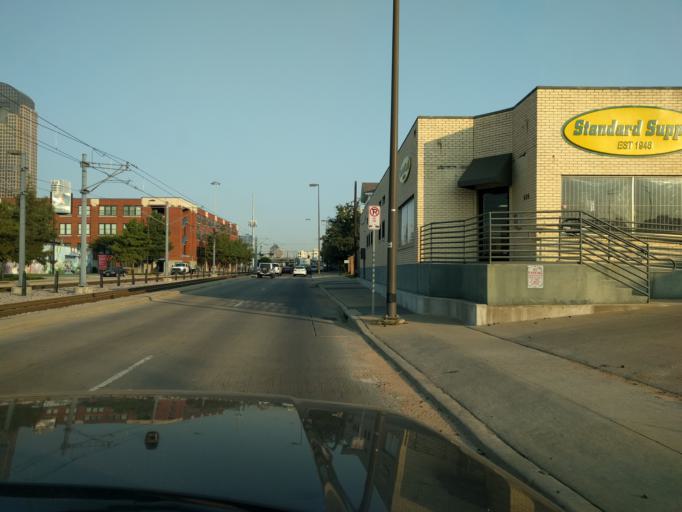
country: US
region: Texas
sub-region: Dallas County
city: Dallas
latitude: 32.7865
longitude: -96.7891
